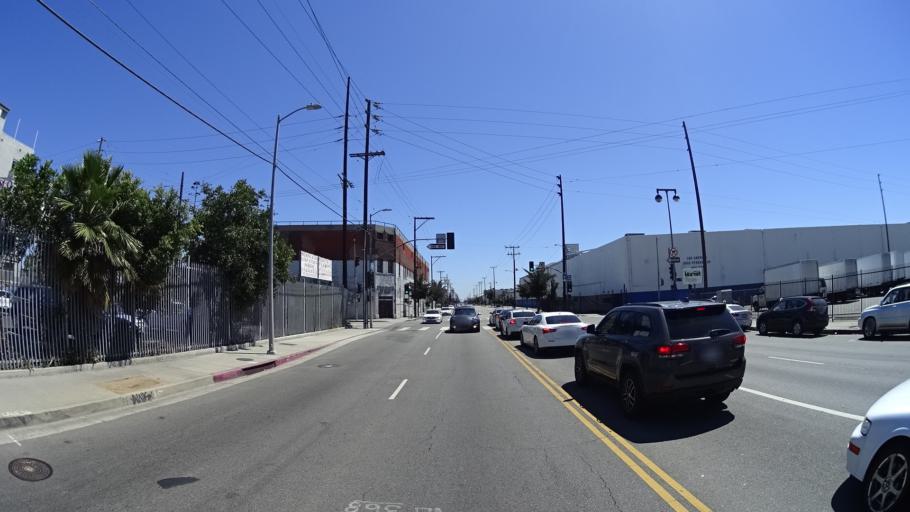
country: US
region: California
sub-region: Los Angeles County
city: Los Angeles
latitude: 34.0436
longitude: -118.2381
